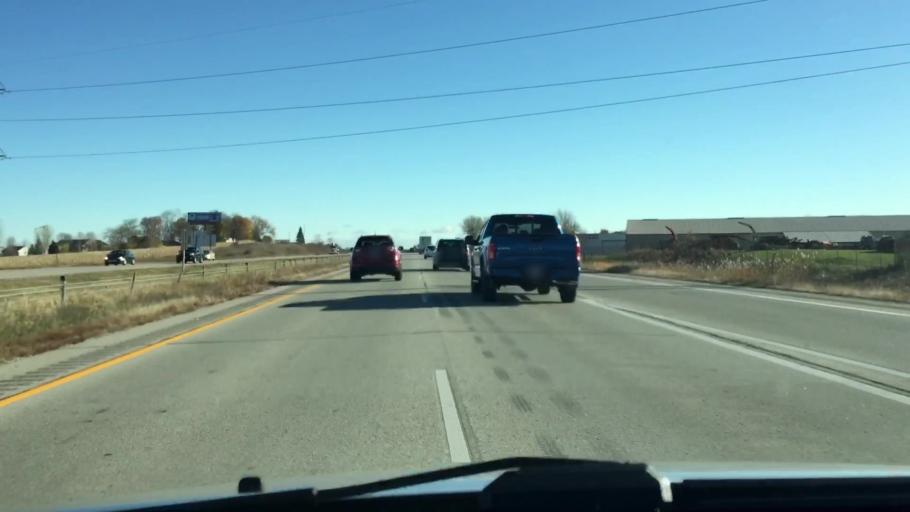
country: US
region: Wisconsin
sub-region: Outagamie County
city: Kaukauna
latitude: 44.3063
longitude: -88.2463
